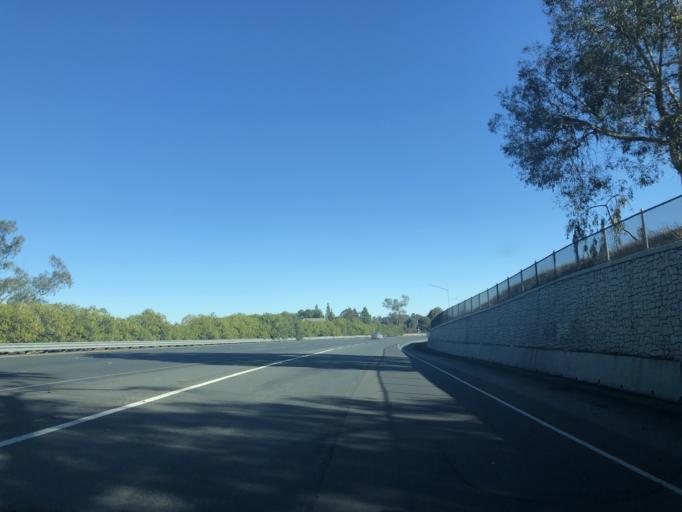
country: US
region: California
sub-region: Contra Costa County
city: Mountain View
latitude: 37.9960
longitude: -122.1172
